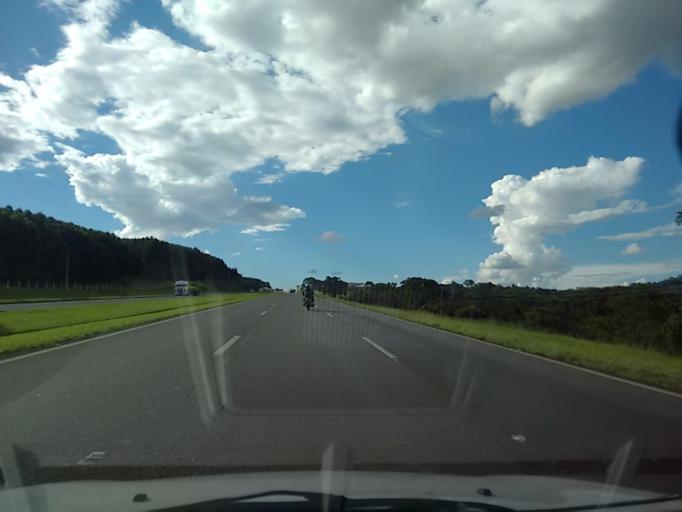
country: BR
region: Sao Paulo
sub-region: Sao Carlos
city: Sao Carlos
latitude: -22.0615
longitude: -47.8512
